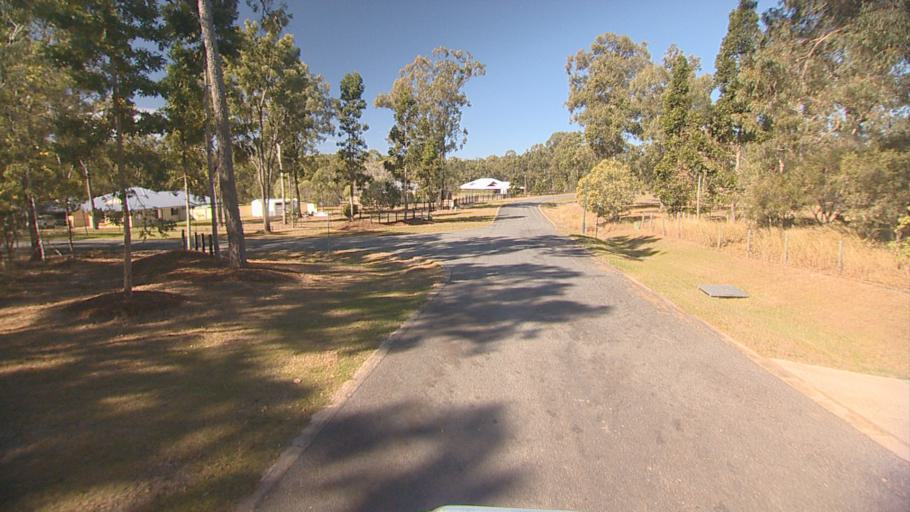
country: AU
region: Queensland
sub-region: Logan
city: North Maclean
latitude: -27.7334
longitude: 152.9645
